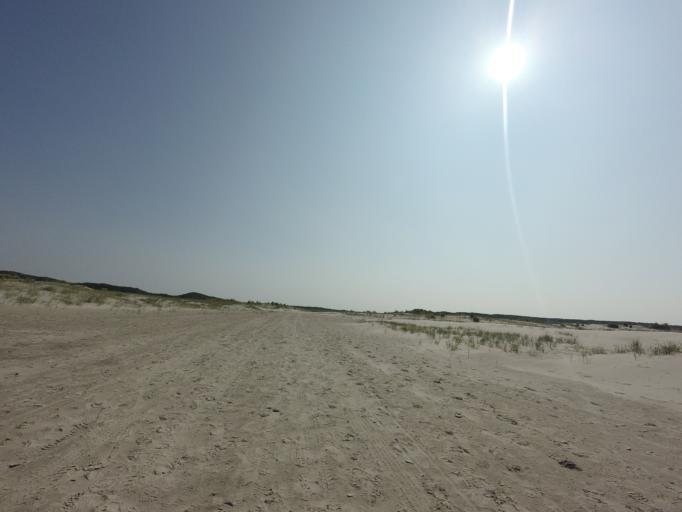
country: NL
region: Friesland
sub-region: Gemeente Schiermonnikoog
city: Schiermonnikoog
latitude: 53.5027
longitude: 6.2457
